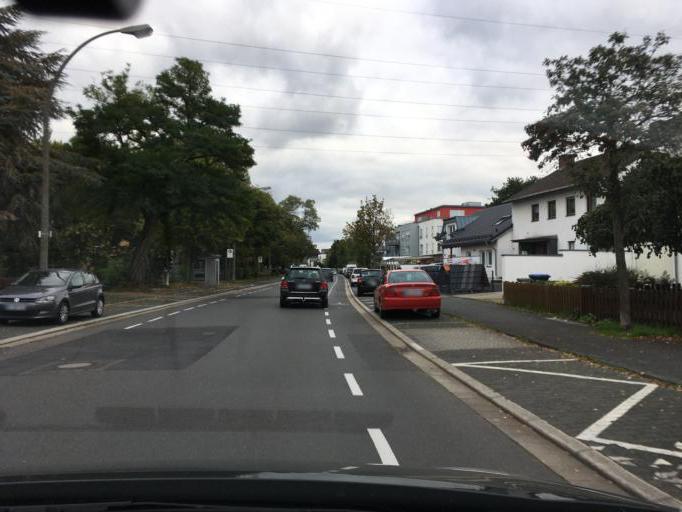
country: DE
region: North Rhine-Westphalia
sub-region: Regierungsbezirk Koln
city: Konigswinter
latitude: 50.6623
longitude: 7.1805
